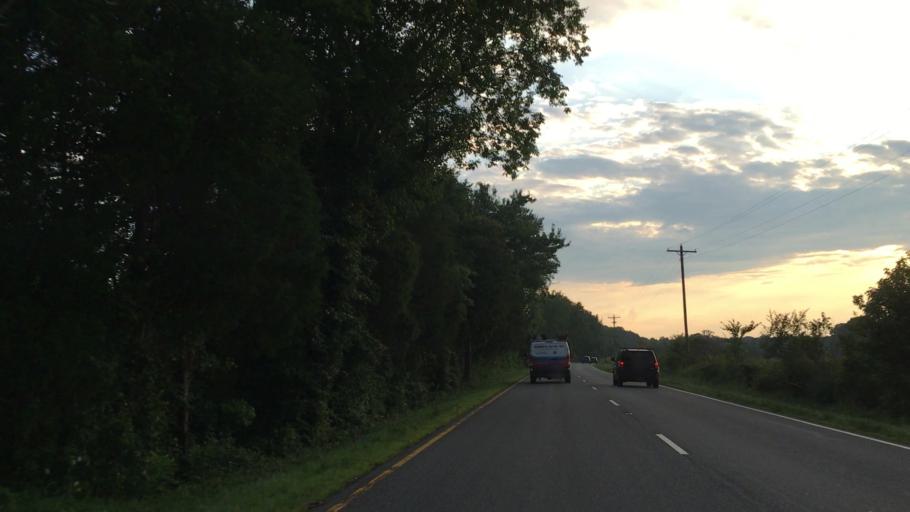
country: US
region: Virginia
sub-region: Spotsylvania County
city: Spotsylvania
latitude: 38.3104
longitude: -77.6649
